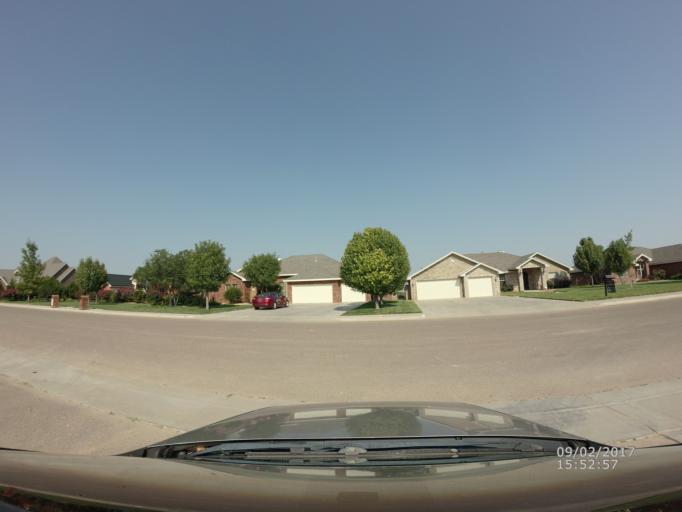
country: US
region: New Mexico
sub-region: Curry County
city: Clovis
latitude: 34.4501
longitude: -103.1885
